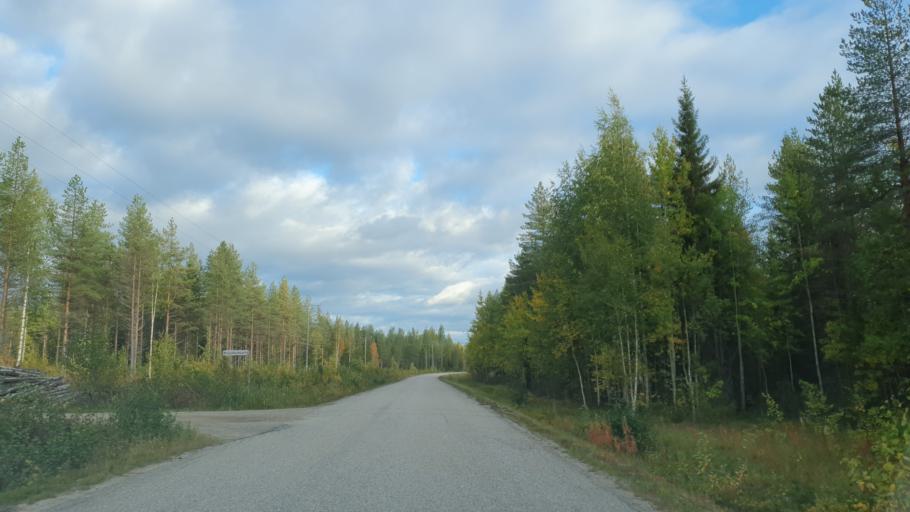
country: FI
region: Kainuu
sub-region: Kehys-Kainuu
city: Kuhmo
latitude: 63.9216
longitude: 30.0491
